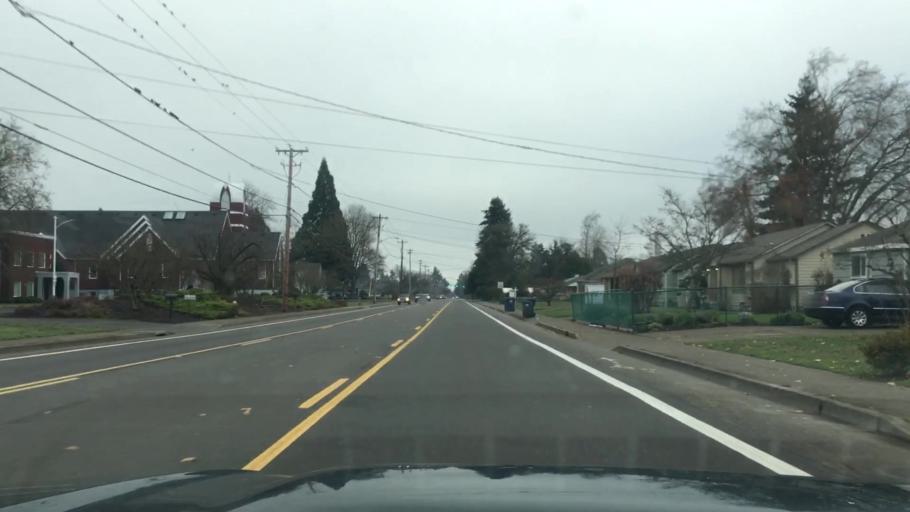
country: US
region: Oregon
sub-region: Lane County
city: Eugene
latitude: 44.0700
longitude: -123.1730
